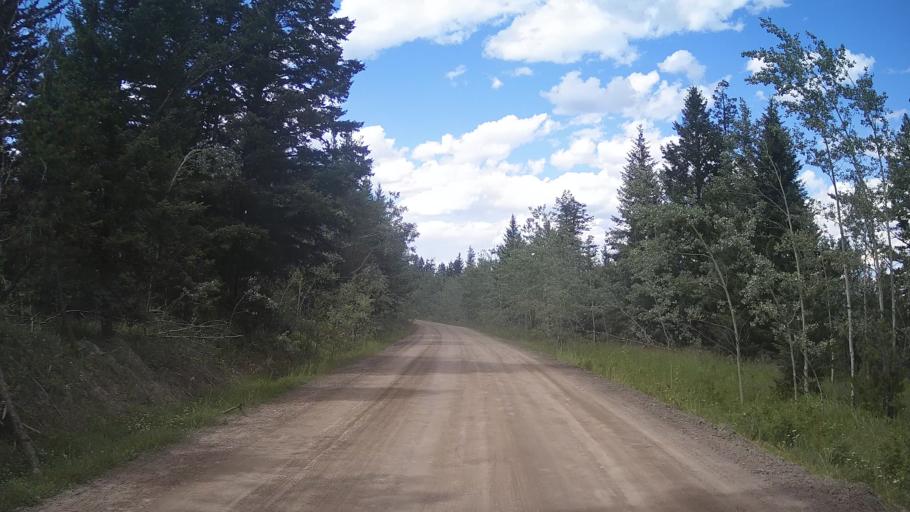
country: CA
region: British Columbia
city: Lillooet
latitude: 51.3320
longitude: -121.8963
